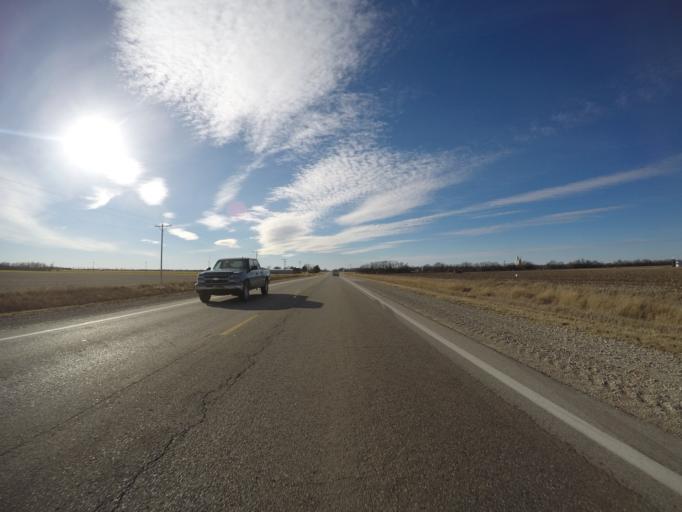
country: US
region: Kansas
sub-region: McPherson County
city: McPherson
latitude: 38.3772
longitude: -97.5247
